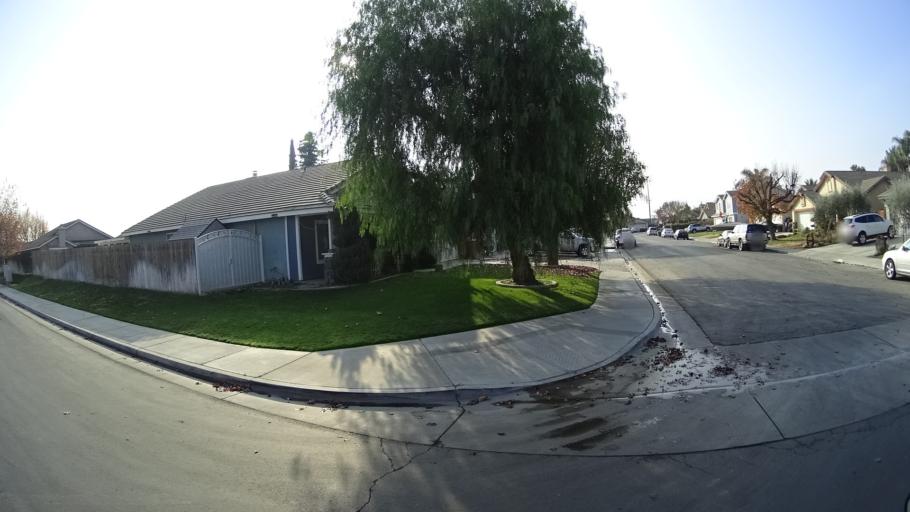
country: US
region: California
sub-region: Kern County
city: Greenfield
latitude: 35.2979
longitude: -119.0685
